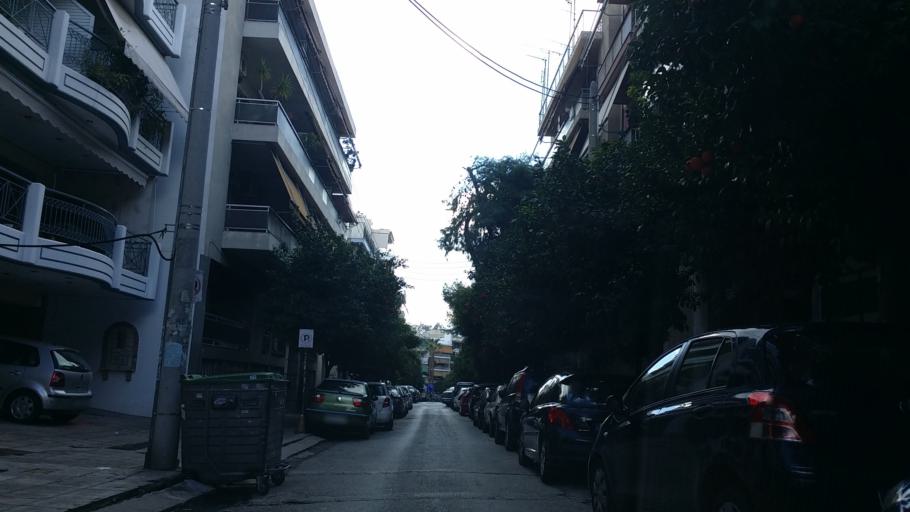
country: GR
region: Attica
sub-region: Nomos Piraios
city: Korydallos
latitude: 37.9794
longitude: 23.6475
